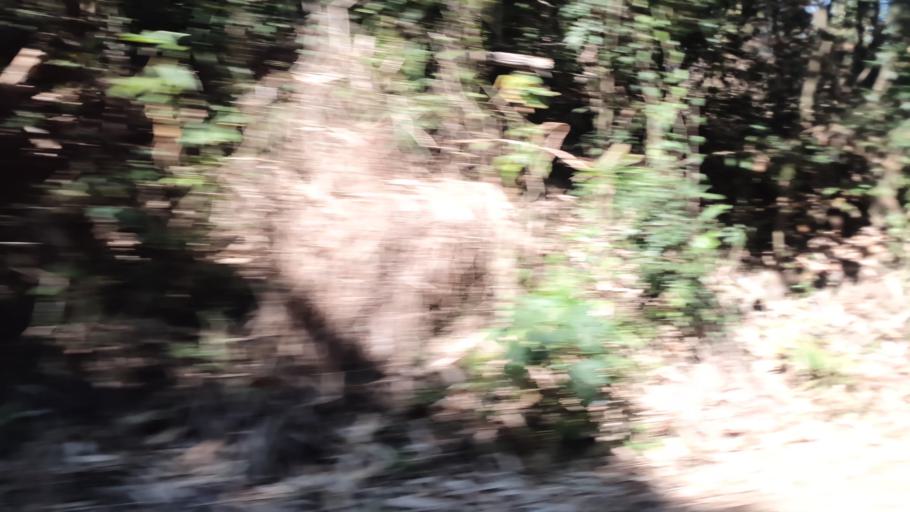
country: TW
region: Taiwan
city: Yujing
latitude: 23.0464
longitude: 120.3666
